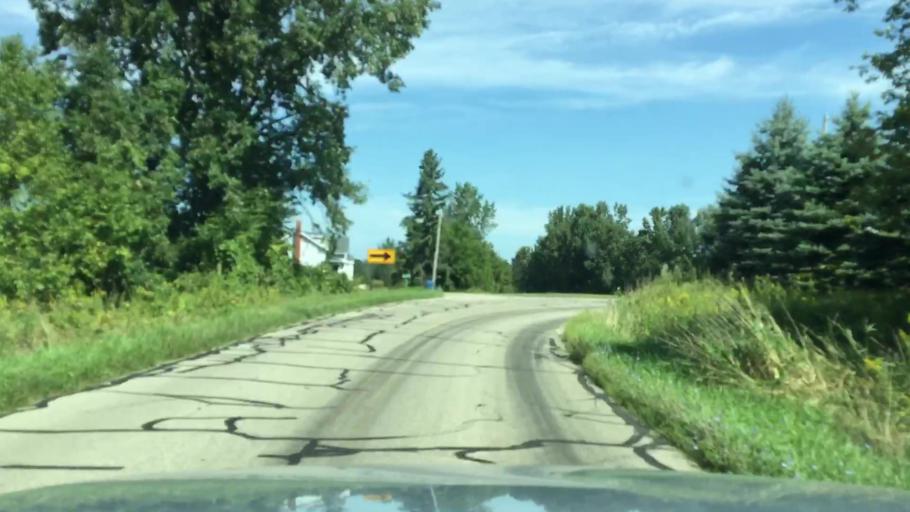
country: US
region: Michigan
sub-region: Lenawee County
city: Manitou Beach-Devils Lake
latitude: 41.9966
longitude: -84.3251
